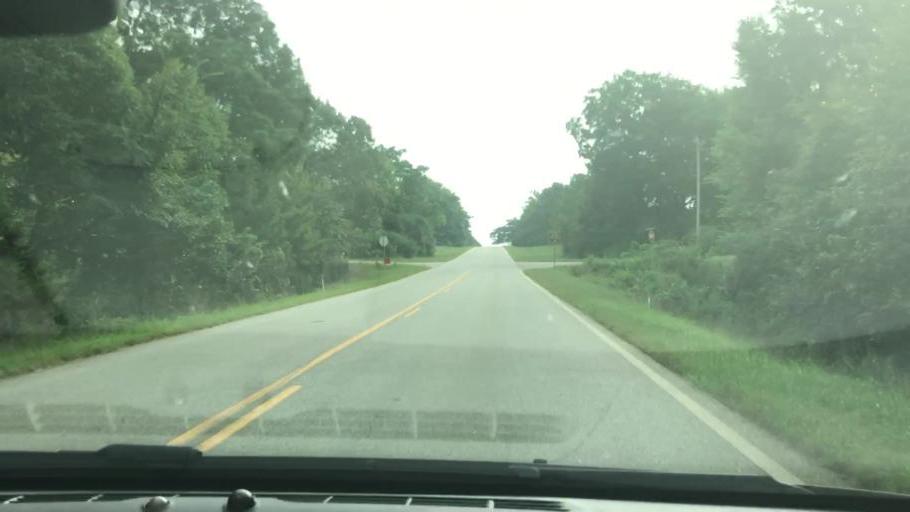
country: US
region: Georgia
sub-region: Stewart County
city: Lumpkin
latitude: 32.0225
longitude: -84.9146
